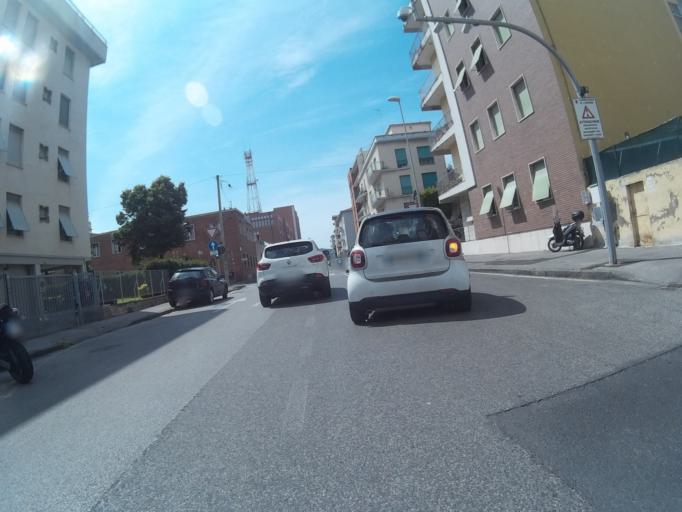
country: IT
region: Tuscany
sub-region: Provincia di Livorno
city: Livorno
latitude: 43.5403
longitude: 10.3209
